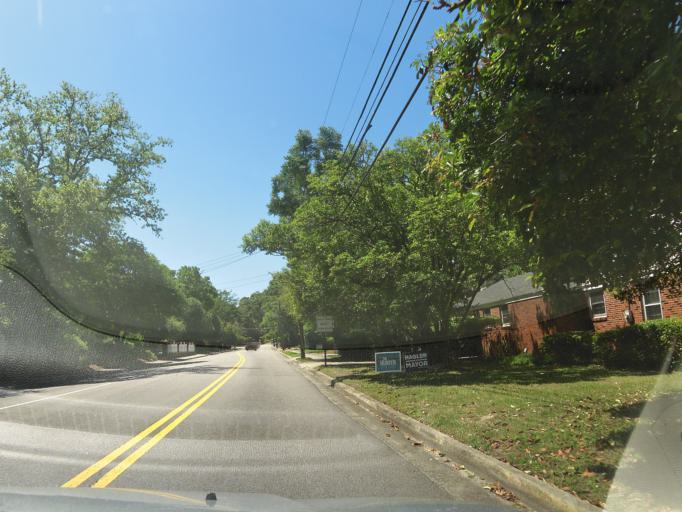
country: US
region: Georgia
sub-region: Richmond County
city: Augusta
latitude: 33.4805
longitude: -82.0312
